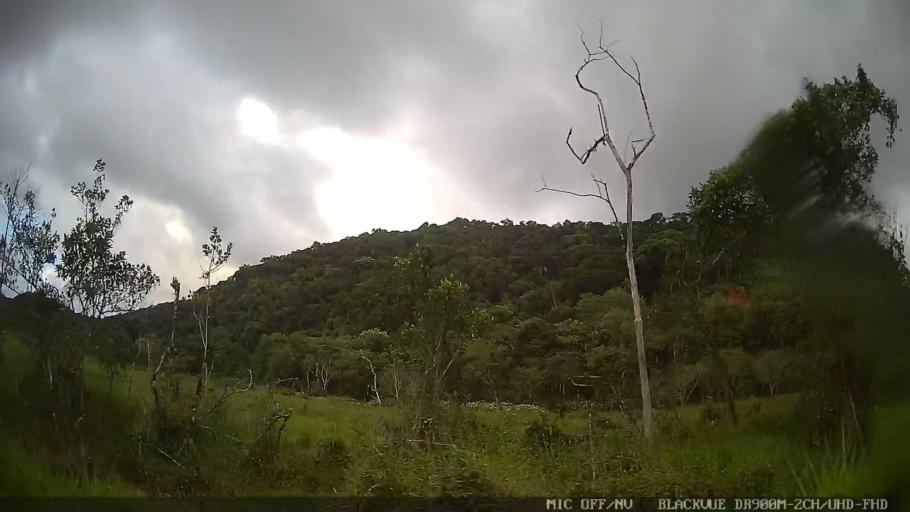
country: BR
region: Sao Paulo
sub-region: Itanhaem
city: Itanhaem
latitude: -24.1409
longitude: -46.7766
